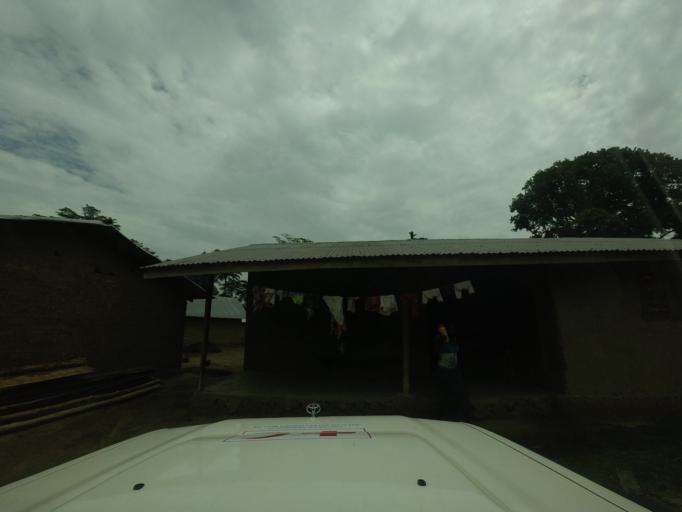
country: SL
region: Eastern Province
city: Buedu
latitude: 8.4211
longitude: -10.2654
